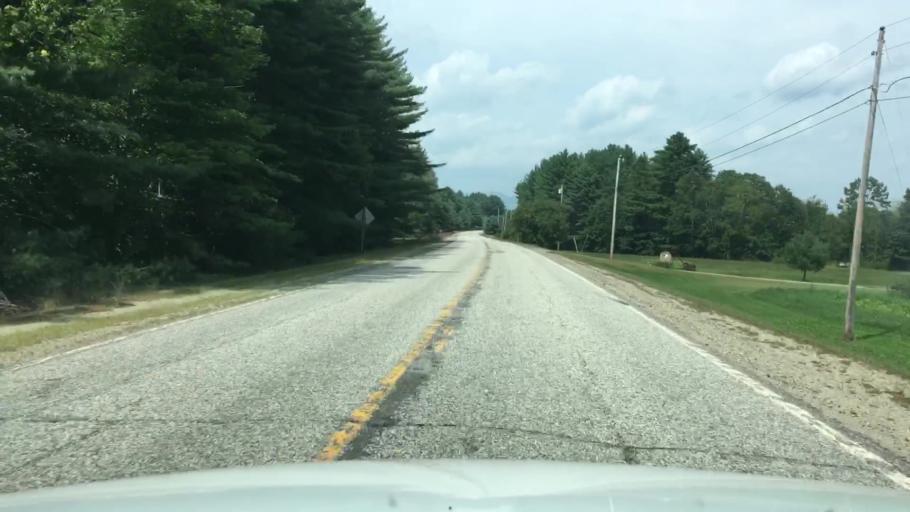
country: US
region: Maine
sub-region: Oxford County
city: Rumford
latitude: 44.5858
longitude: -70.7347
